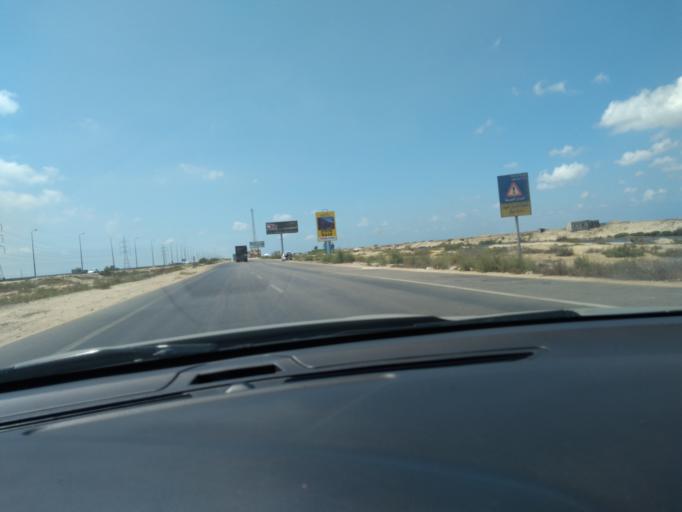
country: EG
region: Muhafazat ad Daqahliyah
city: Al Matariyah
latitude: 31.3568
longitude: 32.0453
